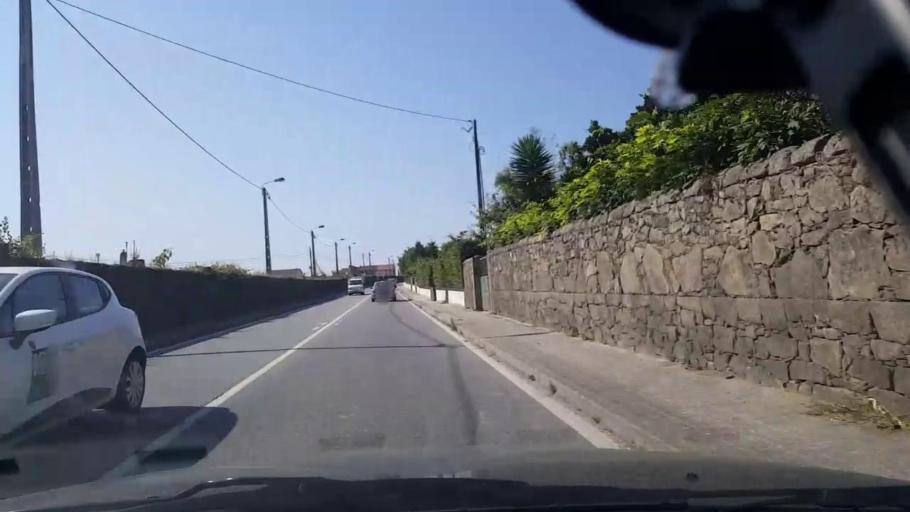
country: PT
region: Porto
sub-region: Povoa de Varzim
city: Pedroso
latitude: 41.3952
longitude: -8.6892
